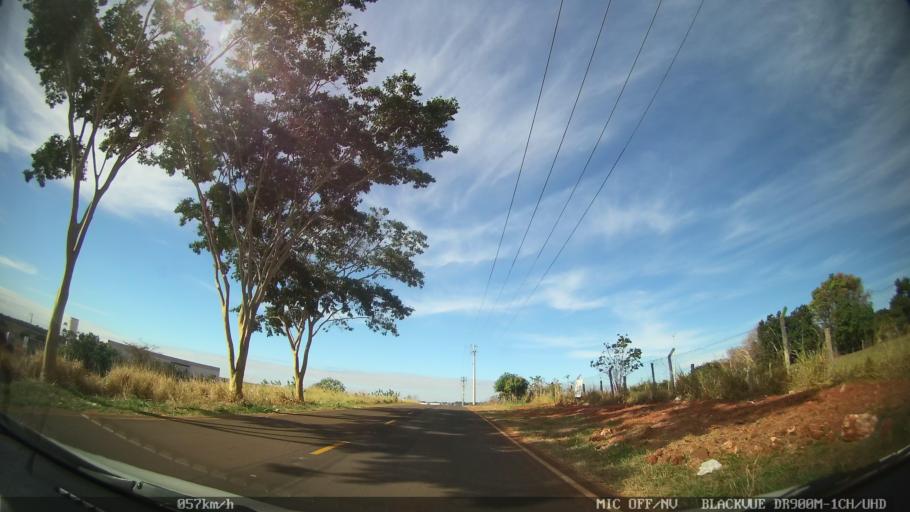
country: BR
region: Sao Paulo
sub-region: Sao Jose Do Rio Preto
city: Sao Jose do Rio Preto
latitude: -20.7993
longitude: -49.3303
